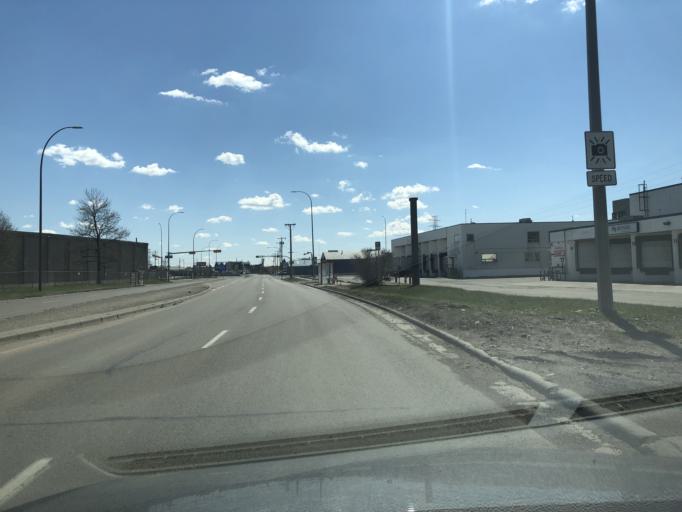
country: CA
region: Alberta
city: Calgary
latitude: 51.0214
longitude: -114.0308
